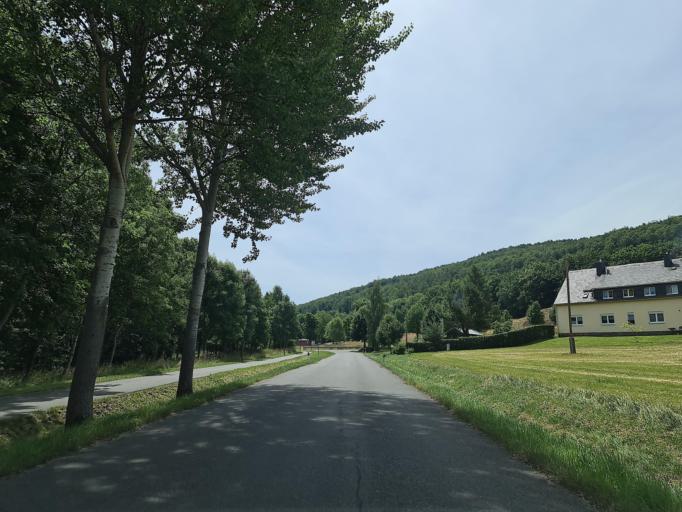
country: DE
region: Saxony
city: Olbernhau
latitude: 50.6452
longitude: 13.3680
